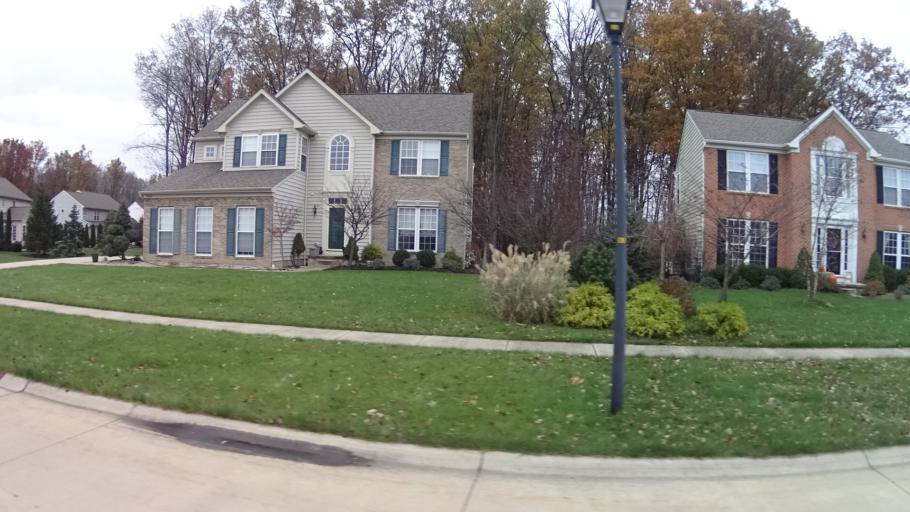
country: US
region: Ohio
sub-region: Cuyahoga County
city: Bay Village
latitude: 41.4827
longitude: -81.9733
